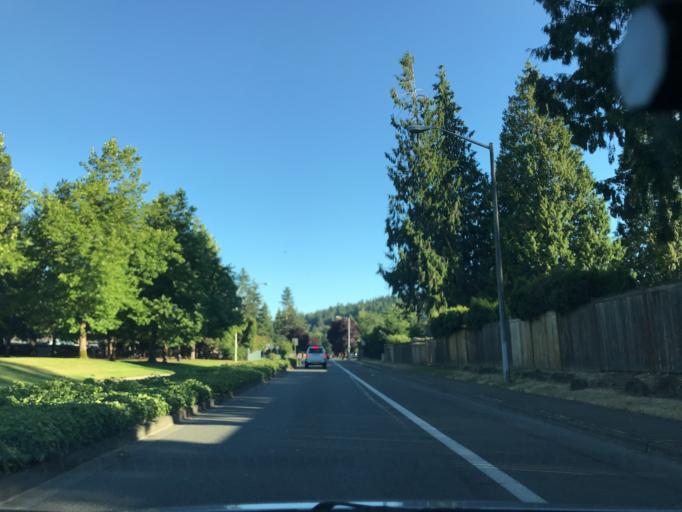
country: US
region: Washington
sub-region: King County
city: Auburn
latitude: 47.2802
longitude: -122.2080
